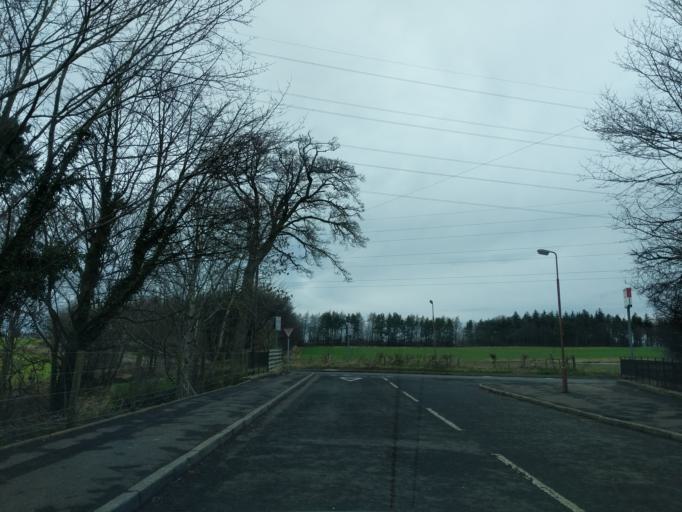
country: GB
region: Scotland
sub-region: Edinburgh
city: Currie
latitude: 55.9007
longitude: -3.3195
